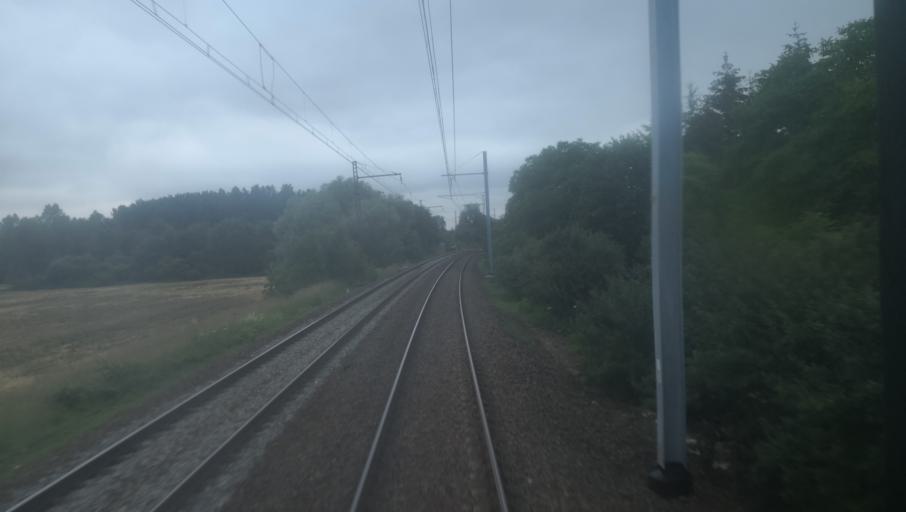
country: FR
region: Centre
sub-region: Departement de l'Indre
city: Sainte-Lizaigne
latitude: 47.0149
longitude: 2.0338
